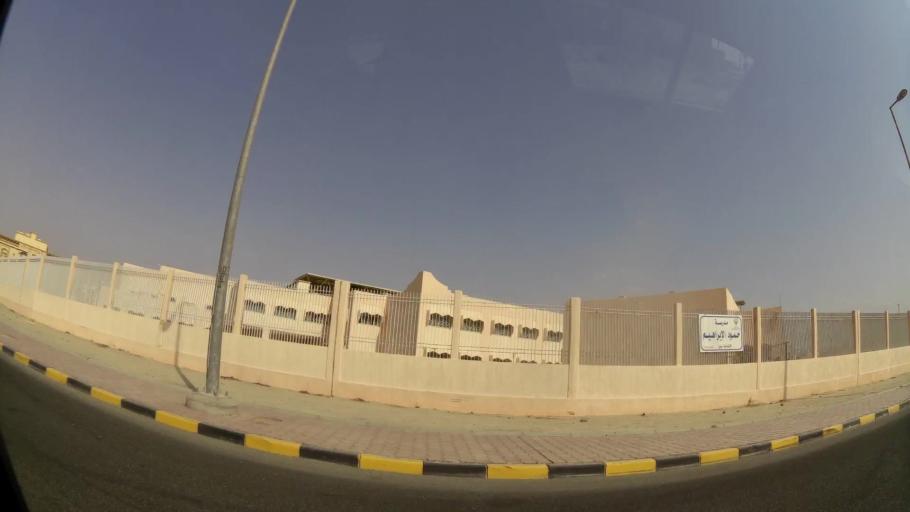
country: KW
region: Muhafazat al Jahra'
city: Al Jahra'
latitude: 29.3364
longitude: 47.7636
